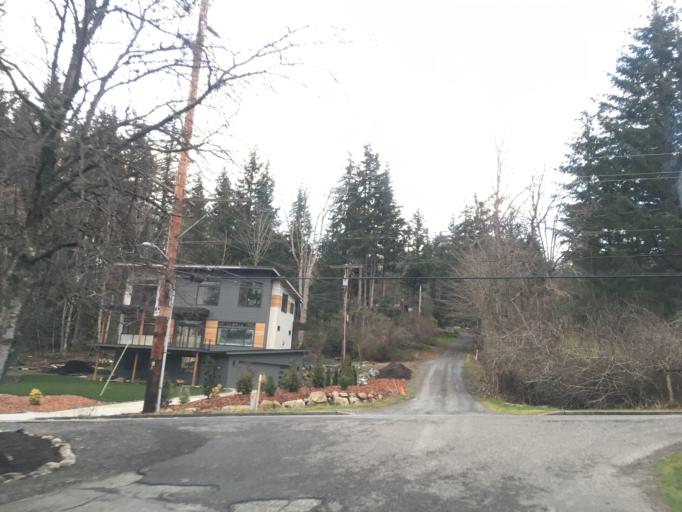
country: US
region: Washington
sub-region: Whatcom County
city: Bellingham
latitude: 48.7203
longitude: -122.4647
